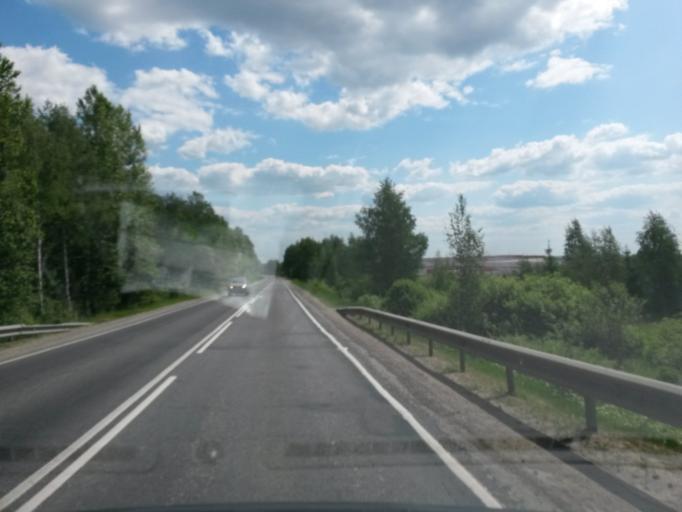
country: RU
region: Jaroslavl
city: Yaroslavl
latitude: 57.5543
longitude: 39.8774
